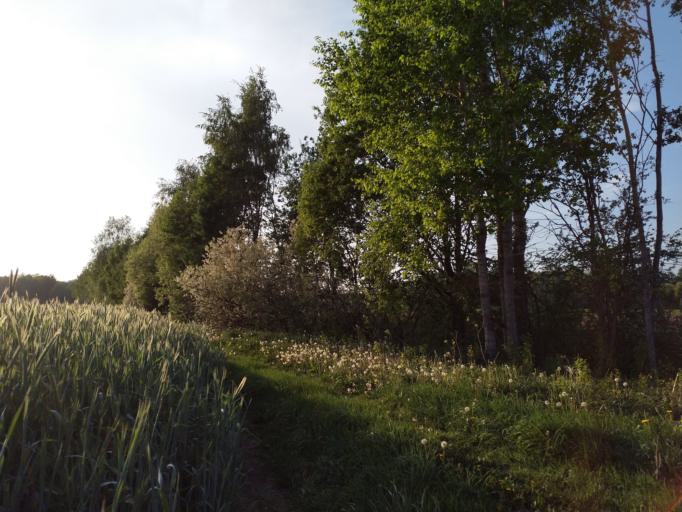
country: LV
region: Aizpute
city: Aizpute
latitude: 56.8276
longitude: 21.7866
